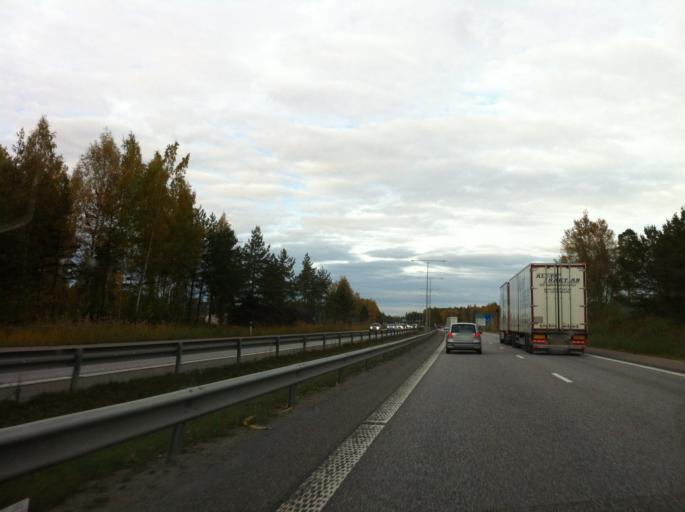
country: SE
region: OErebro
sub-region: Orebro Kommun
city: Orebro
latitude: 59.2283
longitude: 15.1412
